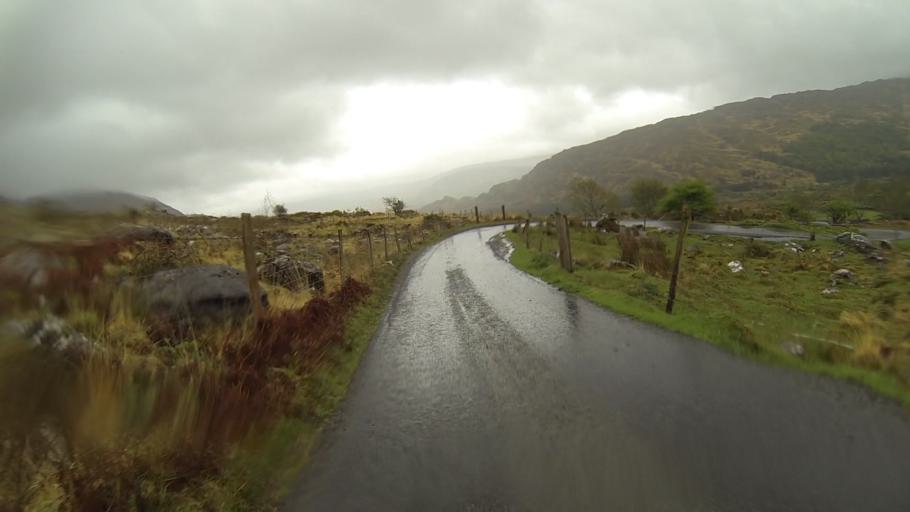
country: IE
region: Munster
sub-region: Ciarrai
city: Kenmare
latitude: 51.9882
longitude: -9.6605
